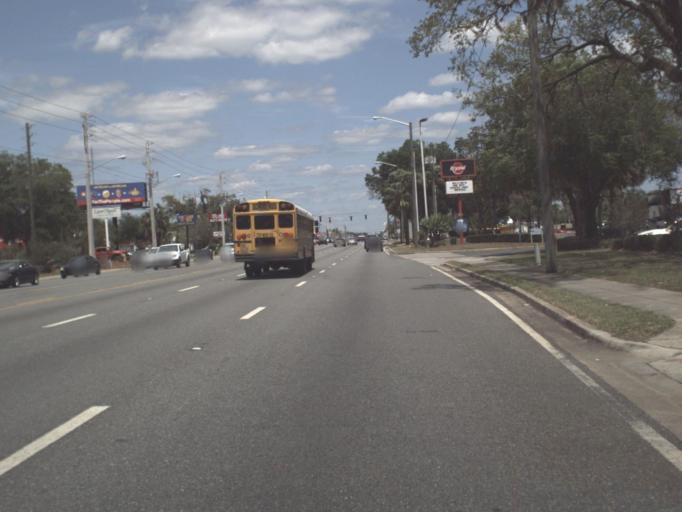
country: US
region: Florida
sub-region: Marion County
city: Ocala
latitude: 29.1680
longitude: -82.1664
